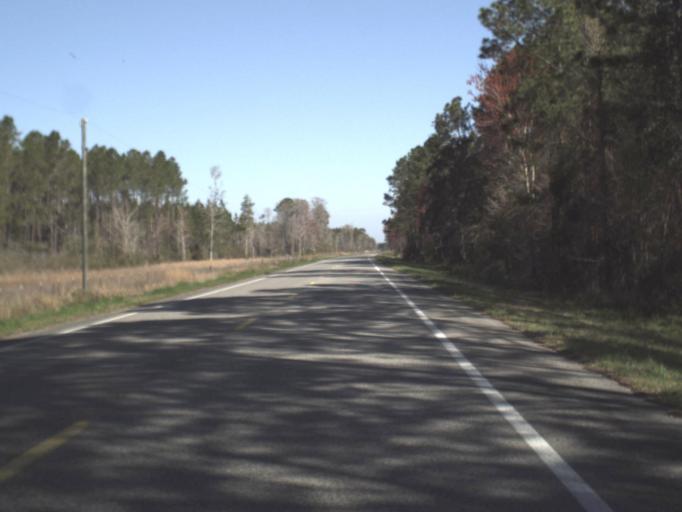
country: US
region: Florida
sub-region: Leon County
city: Woodville
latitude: 30.2499
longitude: -84.0426
